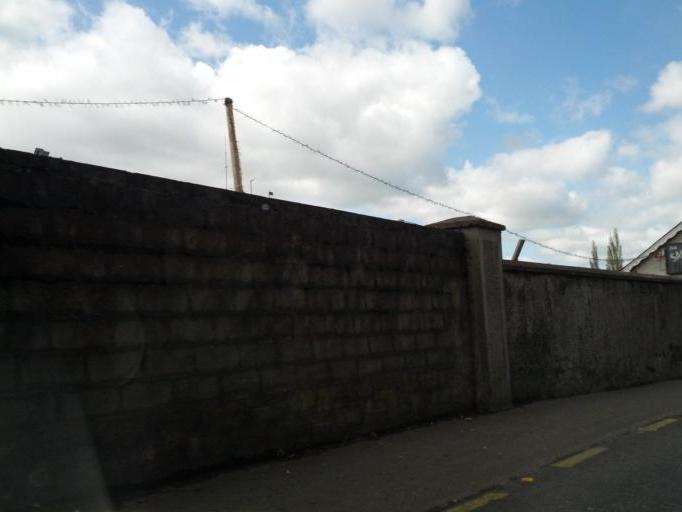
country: IE
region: Leinster
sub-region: Kildare
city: Leixlip
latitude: 53.3621
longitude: -6.4849
